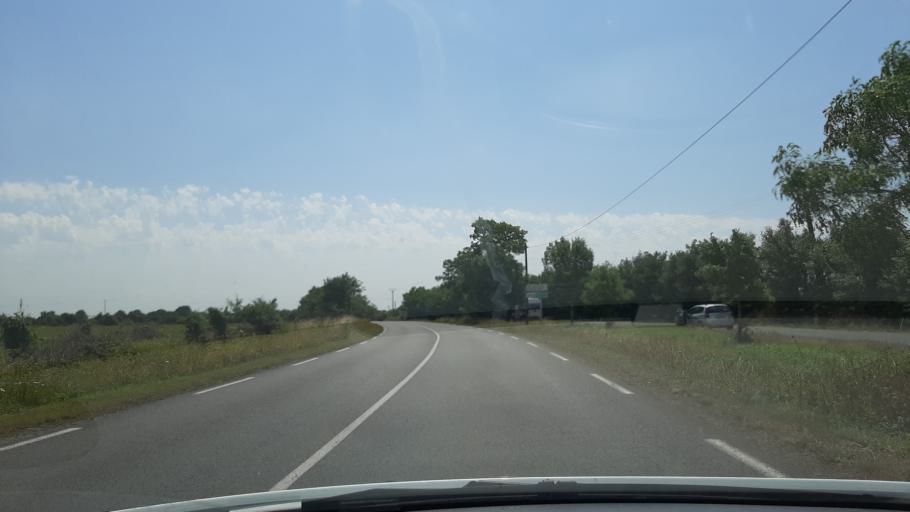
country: FR
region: Pays de la Loire
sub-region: Departement de la Vendee
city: Mouilleron-le-Captif
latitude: 46.7475
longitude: -1.4525
